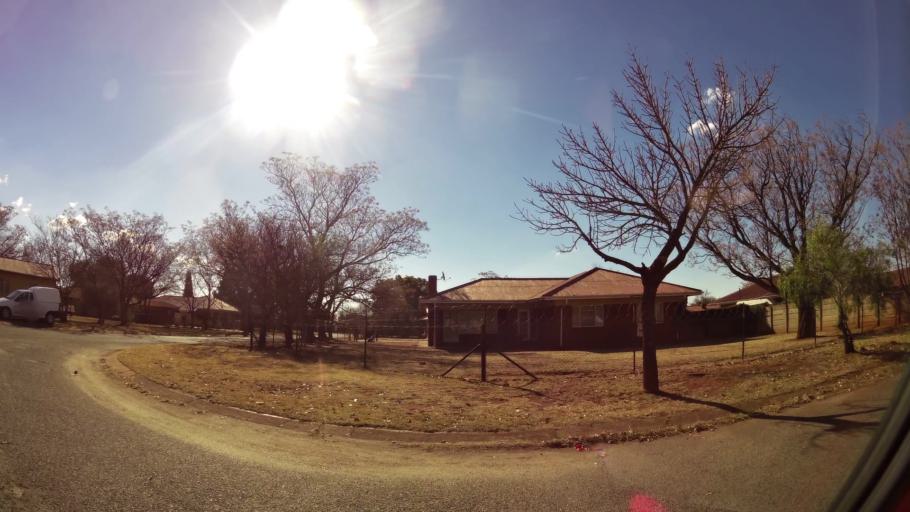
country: ZA
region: Gauteng
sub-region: West Rand District Municipality
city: Carletonville
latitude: -26.3649
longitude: 27.3623
